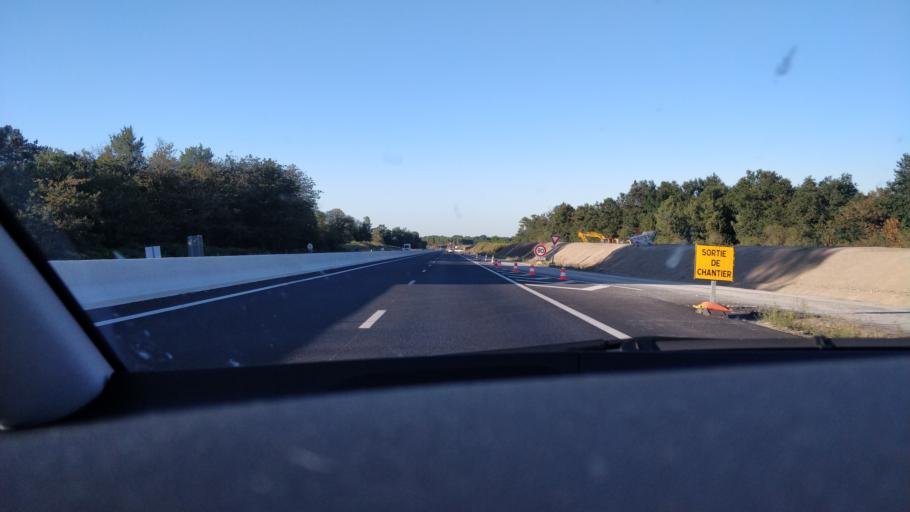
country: FR
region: Poitou-Charentes
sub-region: Departement de la Charente-Maritime
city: Chevanceaux
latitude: 45.3269
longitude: -0.2267
